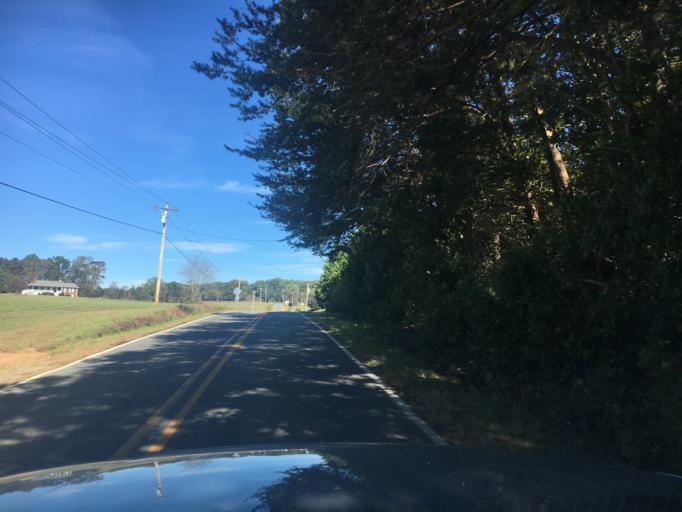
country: US
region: North Carolina
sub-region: Burke County
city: Salem
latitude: 35.6952
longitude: -81.7368
